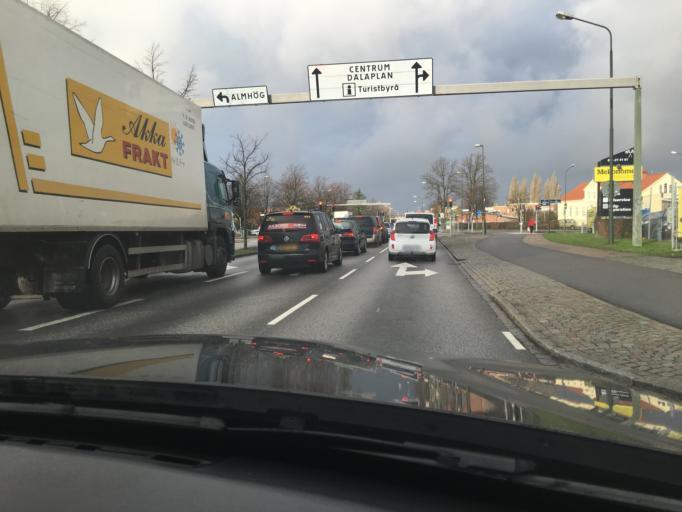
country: SE
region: Skane
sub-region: Malmo
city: Malmoe
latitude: 55.5773
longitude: 13.0251
